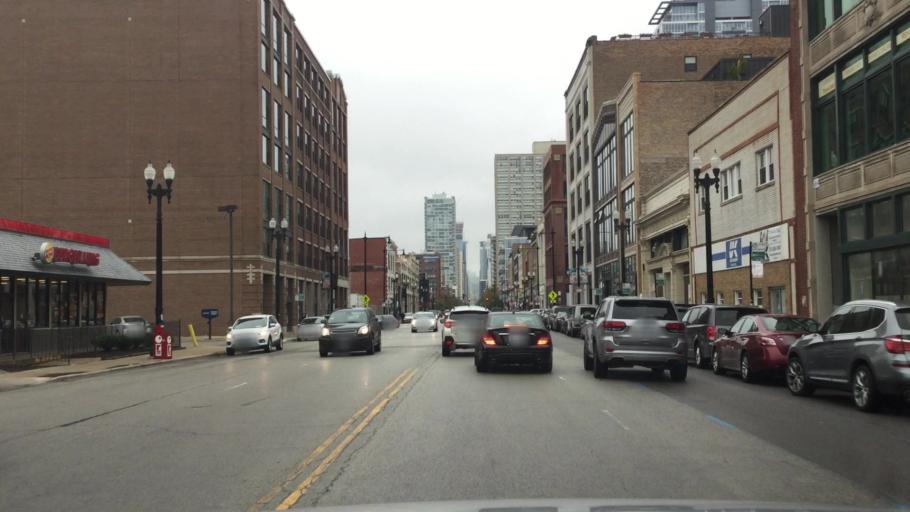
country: US
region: Illinois
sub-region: Cook County
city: Chicago
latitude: 41.8501
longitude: -87.6237
